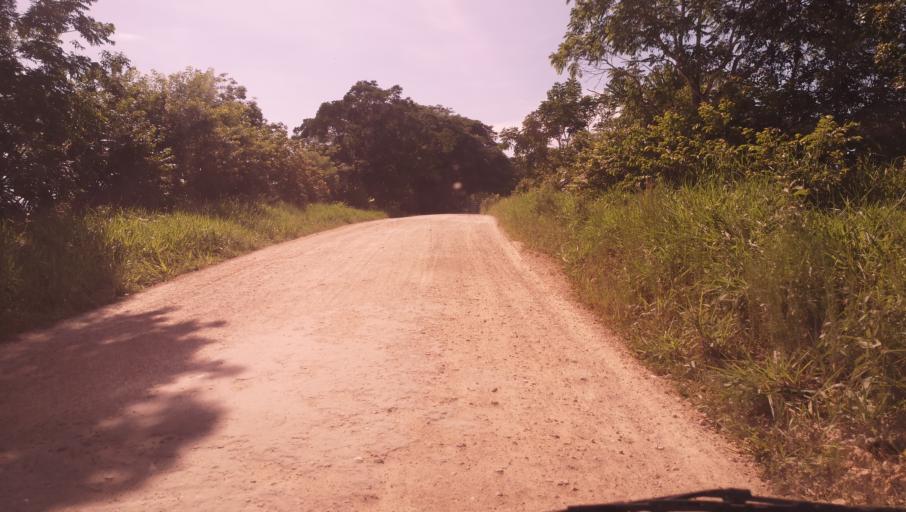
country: GT
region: Peten
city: Dolores
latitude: 16.7208
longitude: -89.3754
